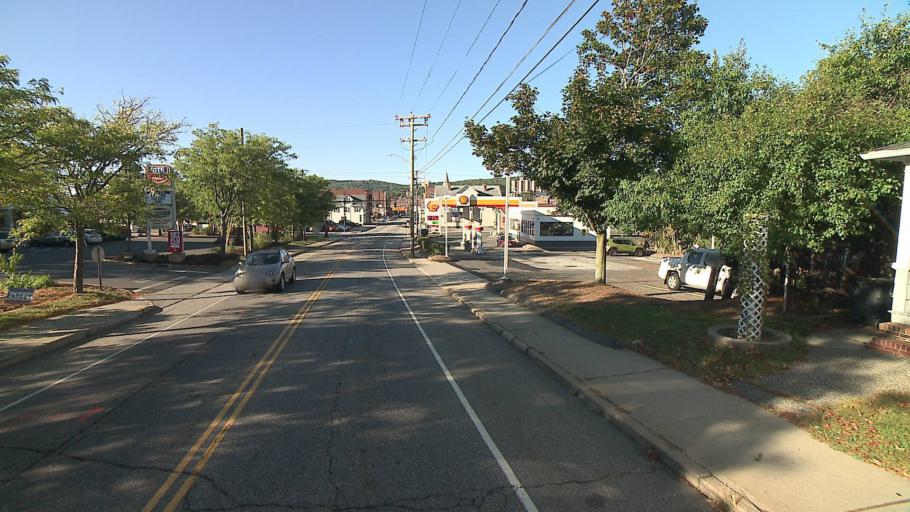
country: US
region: Connecticut
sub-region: Litchfield County
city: Torrington
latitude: 41.8036
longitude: -73.1168
